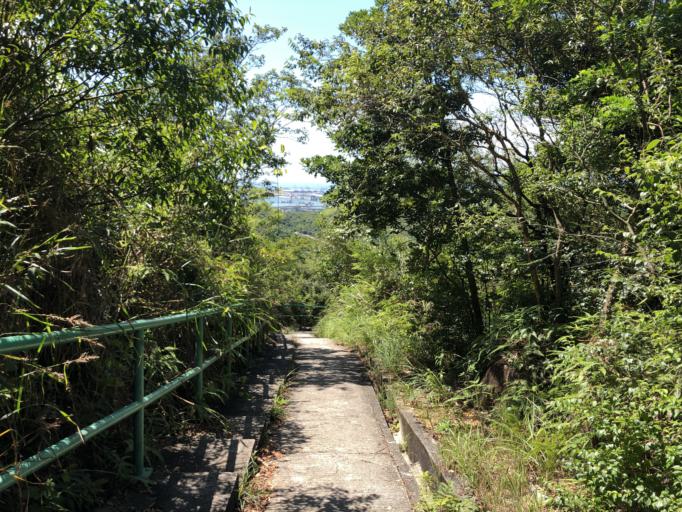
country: HK
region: Tuen Mun
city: Tuen Mun
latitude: 22.2857
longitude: 113.9819
